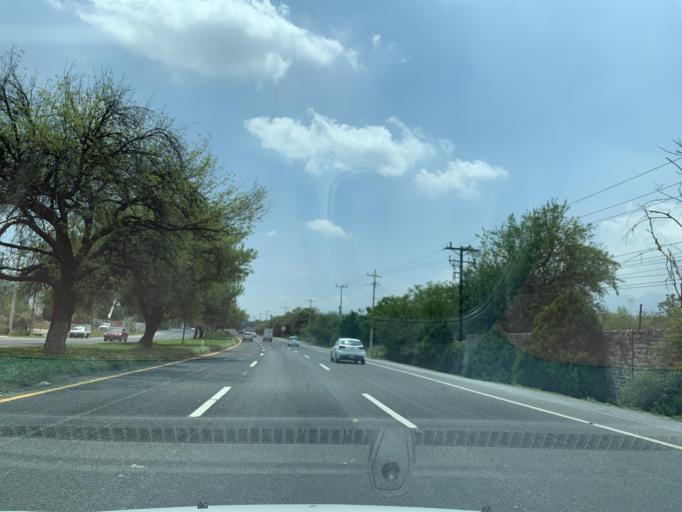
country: MX
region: Nuevo Leon
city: Santiago
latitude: 25.4985
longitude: -100.1903
